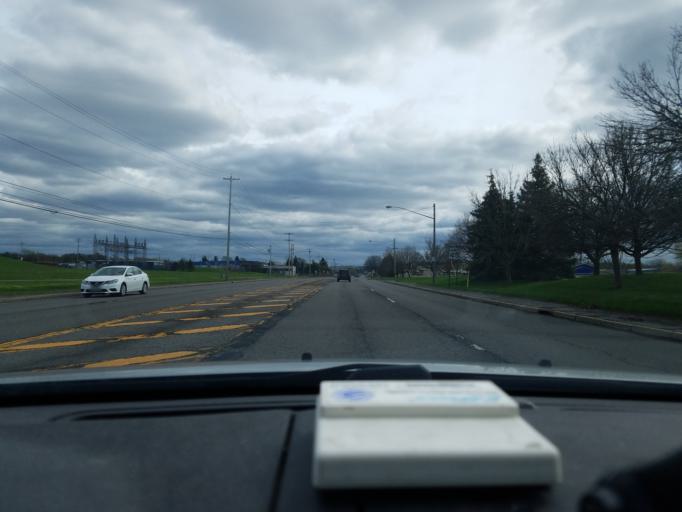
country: US
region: New York
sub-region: Onondaga County
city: East Syracuse
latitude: 43.0836
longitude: -76.0897
